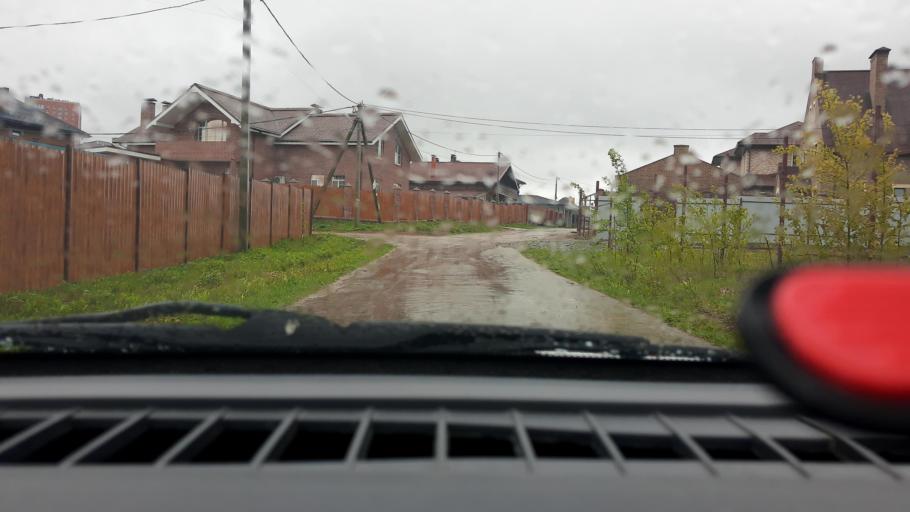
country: RU
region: Nizjnij Novgorod
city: Afonino
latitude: 56.2514
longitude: 44.0330
